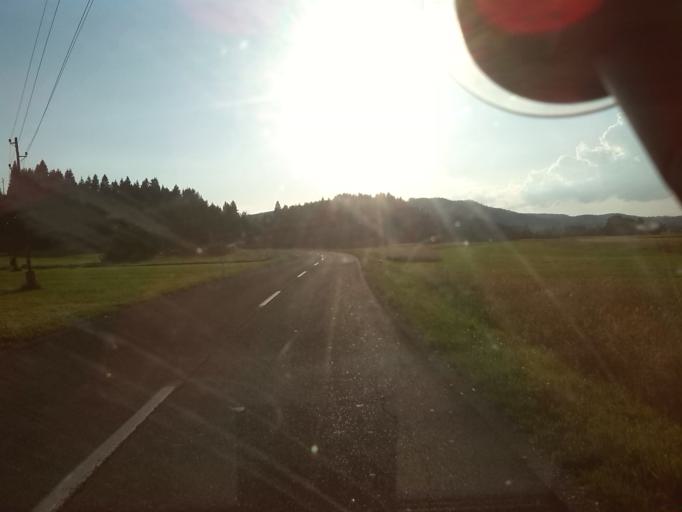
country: SI
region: Bloke
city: Nova Vas
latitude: 45.7733
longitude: 14.4990
